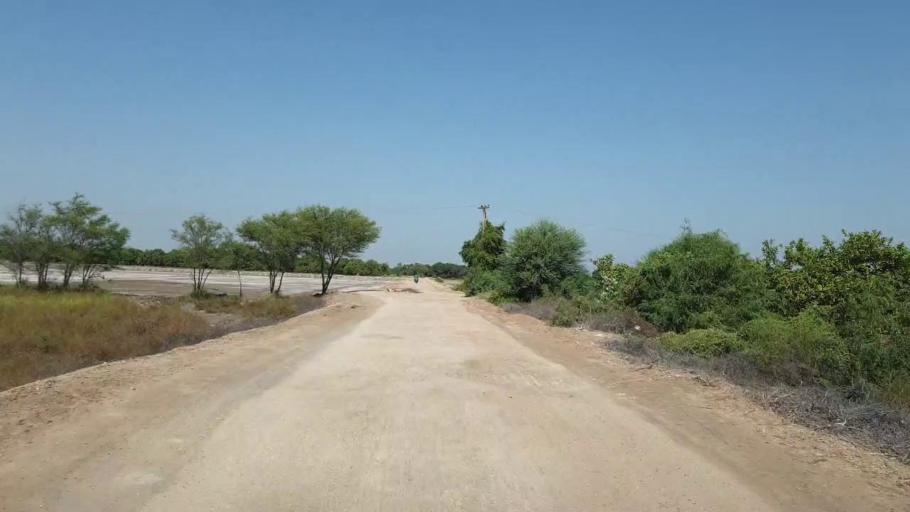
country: PK
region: Sindh
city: Tando Jam
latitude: 25.4189
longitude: 68.4574
